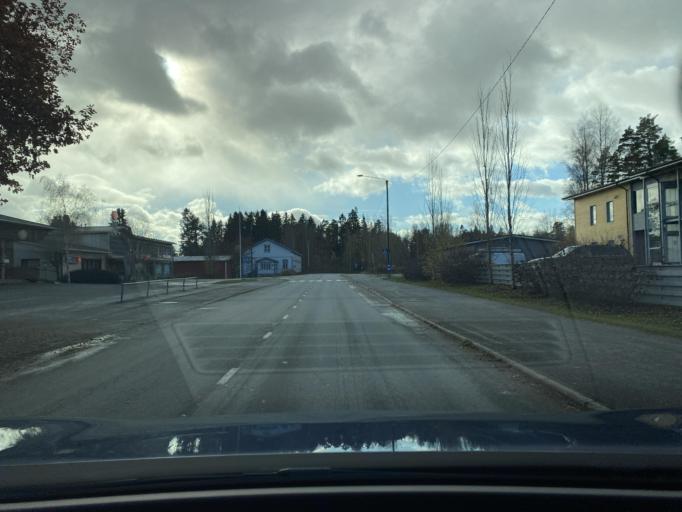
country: FI
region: Varsinais-Suomi
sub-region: Loimaa
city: Aura
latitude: 60.7190
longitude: 22.6031
